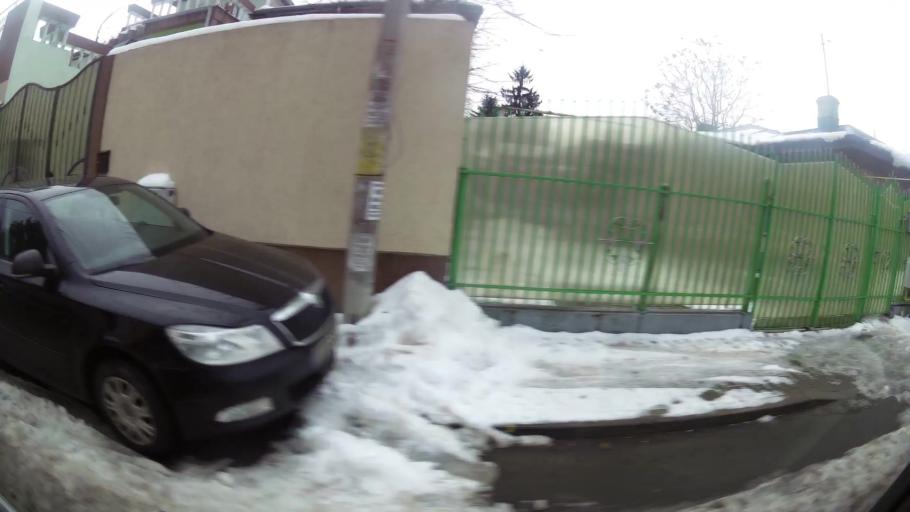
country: RO
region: Bucuresti
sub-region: Municipiul Bucuresti
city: Bucuresti
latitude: 44.4066
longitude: 26.0561
